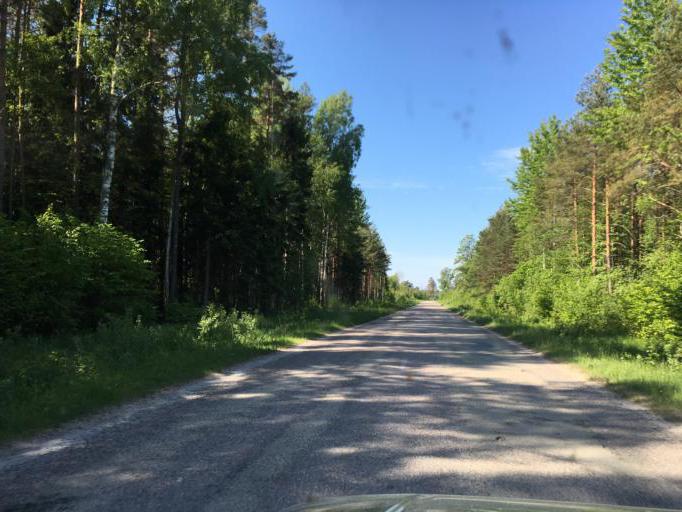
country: LV
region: Ventspils
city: Ventspils
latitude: 57.4856
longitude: 21.7775
